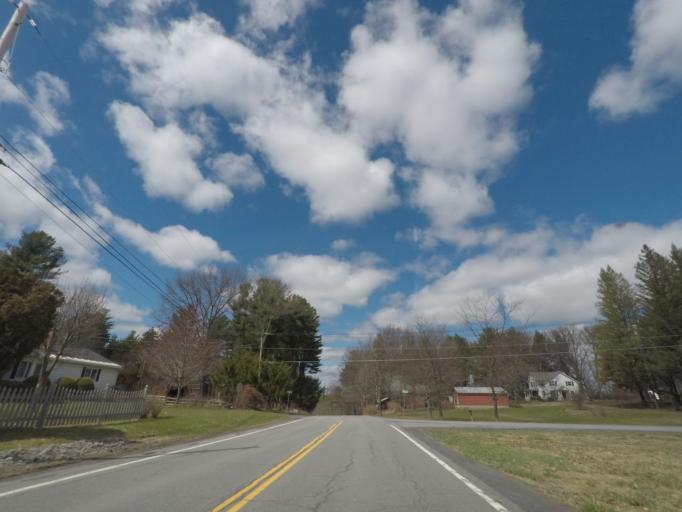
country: US
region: New York
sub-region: Albany County
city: Voorheesville
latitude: 42.6439
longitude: -73.9720
